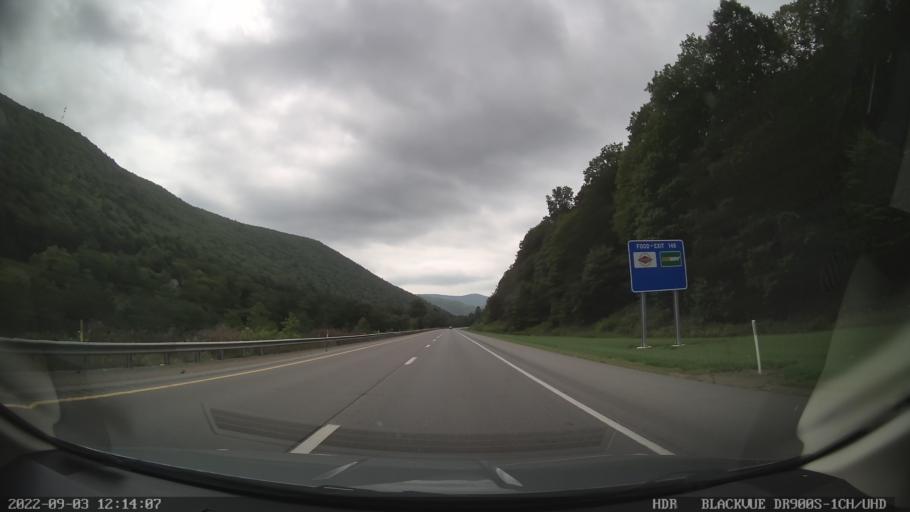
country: US
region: Pennsylvania
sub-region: Lycoming County
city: Garden View
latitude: 41.4074
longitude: -77.0663
